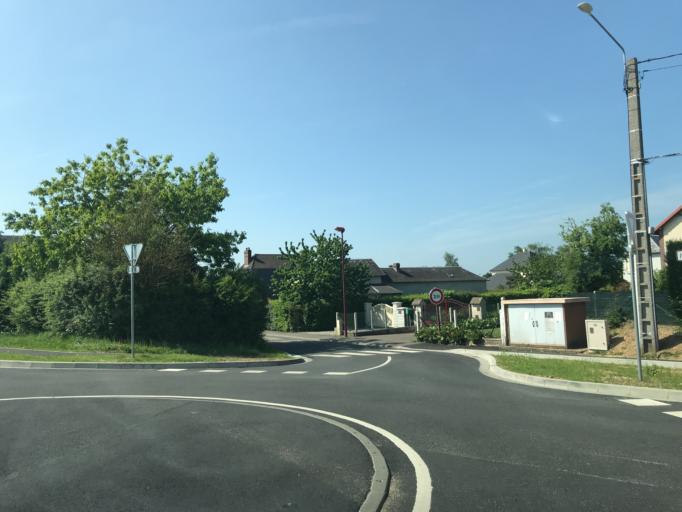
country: FR
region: Haute-Normandie
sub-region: Departement de la Seine-Maritime
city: Belbeuf
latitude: 49.3673
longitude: 1.1582
